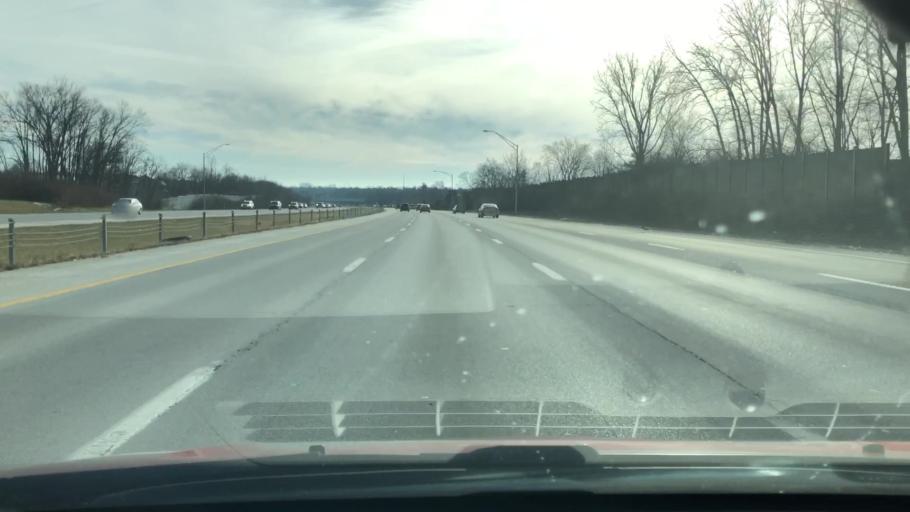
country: US
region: Ohio
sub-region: Greene County
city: Beavercreek
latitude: 39.6918
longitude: -84.0989
